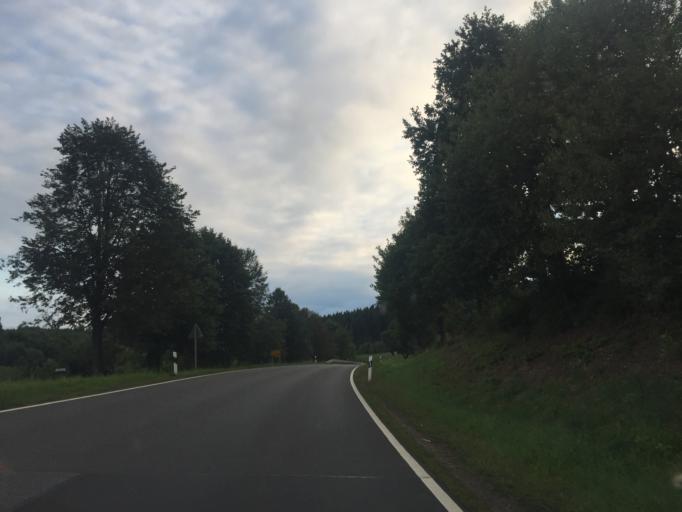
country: DE
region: Bavaria
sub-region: Upper Palatinate
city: Windischeschenbach
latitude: 49.7941
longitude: 12.1535
